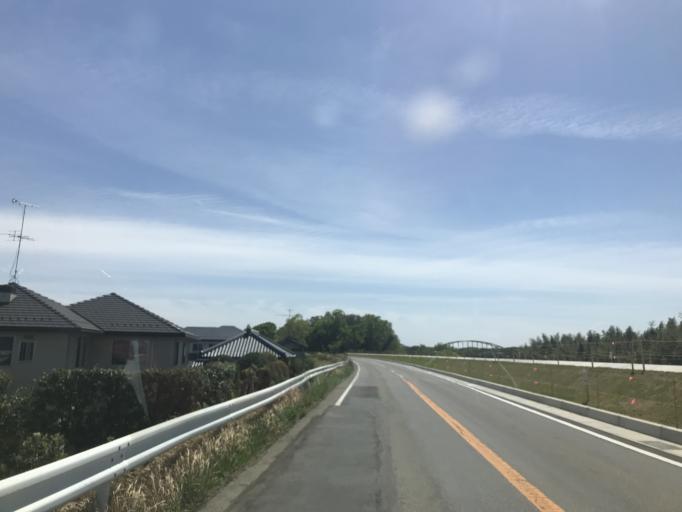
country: JP
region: Ibaraki
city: Mitsukaido
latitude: 36.0672
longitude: 139.9801
